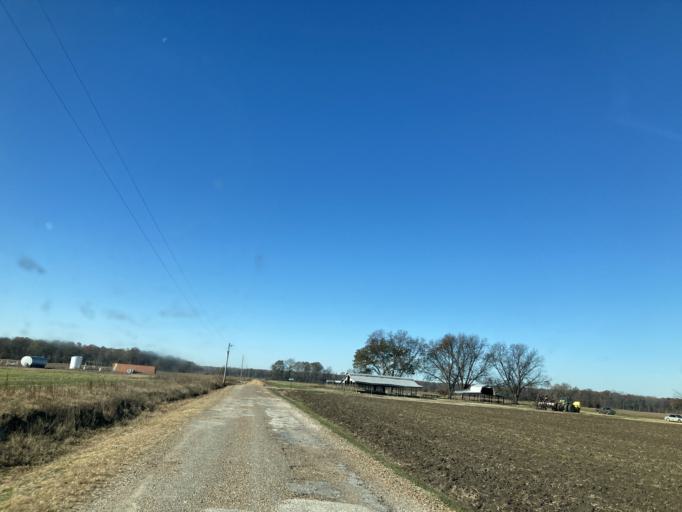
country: US
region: Mississippi
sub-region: Sharkey County
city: Rolling Fork
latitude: 32.8574
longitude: -90.7090
